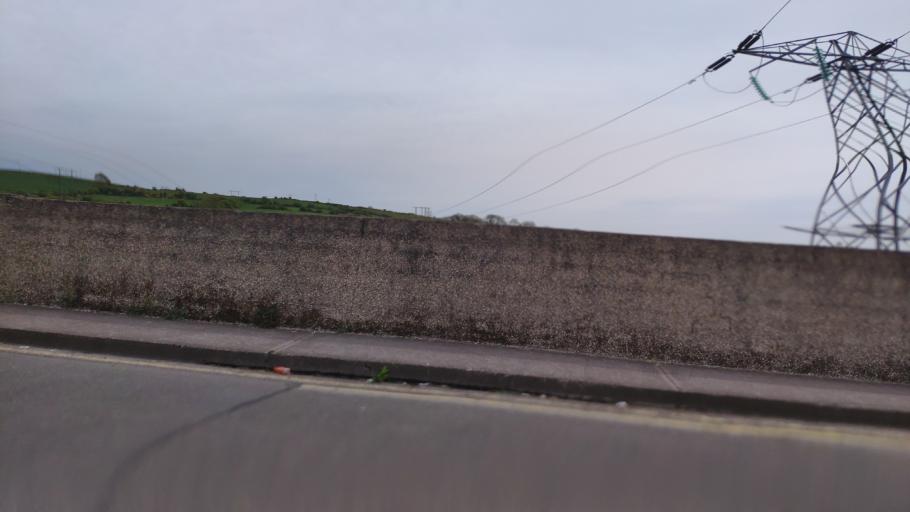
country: IE
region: Munster
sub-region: County Cork
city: Cork
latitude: 51.9225
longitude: -8.4589
